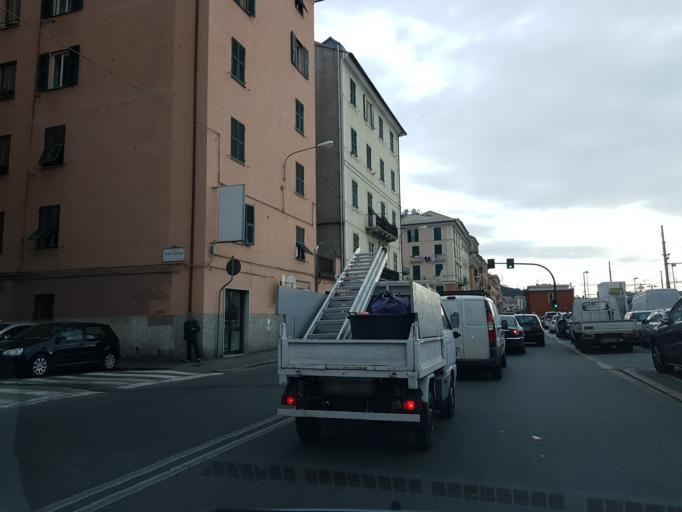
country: IT
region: Liguria
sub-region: Provincia di Genova
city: San Teodoro
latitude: 44.4231
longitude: 8.8461
